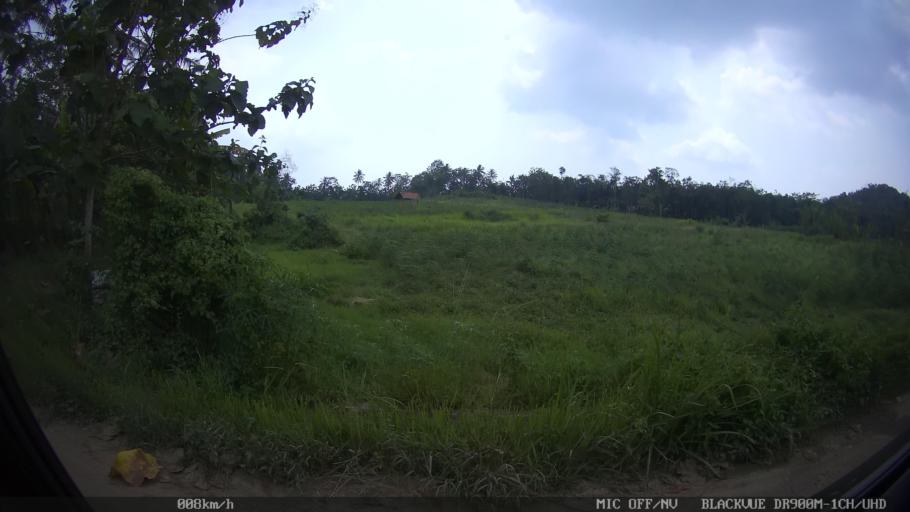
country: ID
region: Lampung
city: Gadingrejo
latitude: -5.3893
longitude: 105.0362
